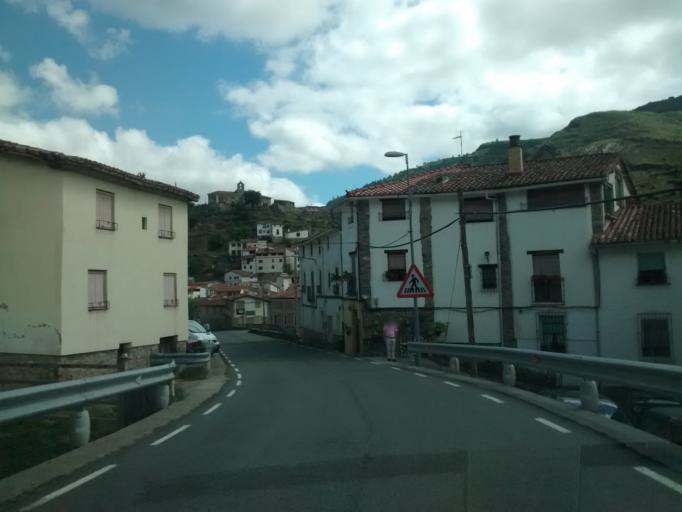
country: ES
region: La Rioja
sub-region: Provincia de La Rioja
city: Soto en Cameros
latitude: 42.2848
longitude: -2.4275
